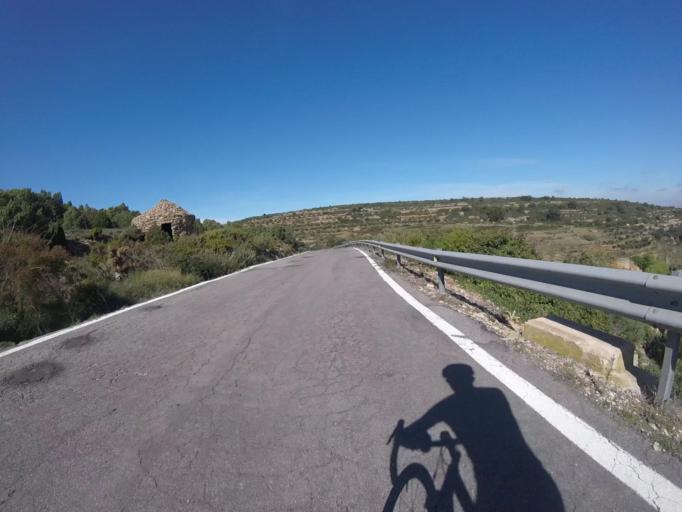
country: ES
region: Valencia
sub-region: Provincia de Castello
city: Sarratella
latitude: 40.3241
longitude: 0.0281
